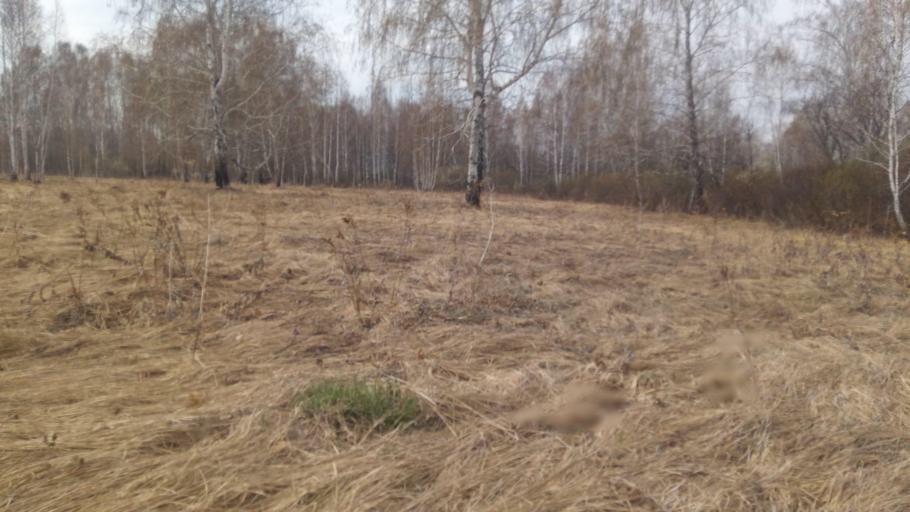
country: RU
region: Chelyabinsk
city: Timiryazevskiy
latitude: 54.9972
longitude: 60.8478
